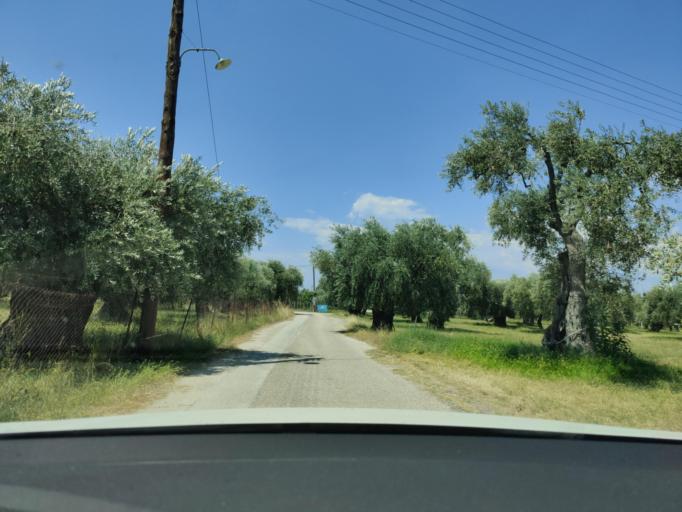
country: GR
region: East Macedonia and Thrace
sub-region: Nomos Kavalas
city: Prinos
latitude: 40.7691
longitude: 24.5974
